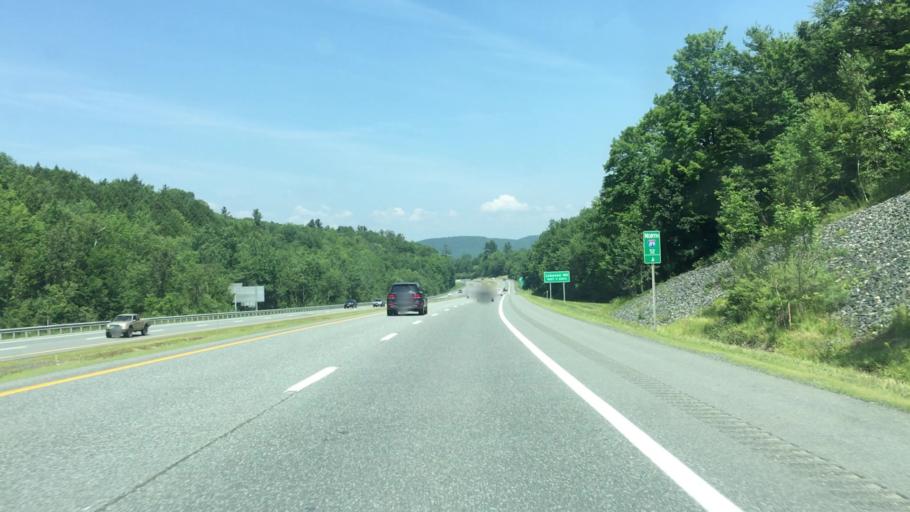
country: US
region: New Hampshire
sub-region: Grafton County
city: Enfield
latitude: 43.6176
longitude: -72.1956
